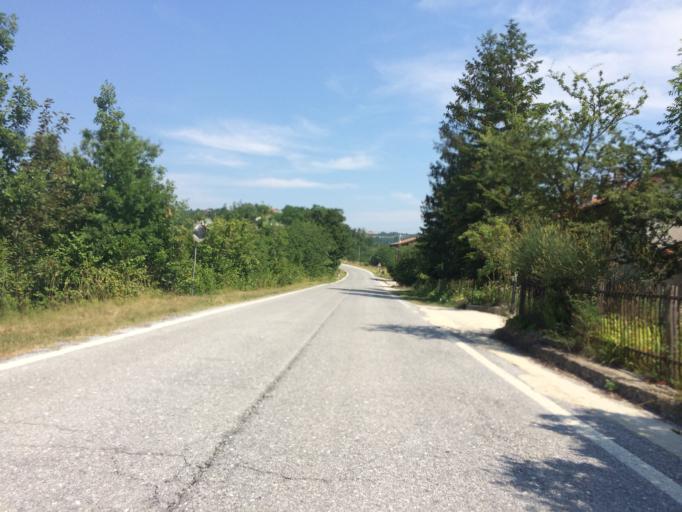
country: IT
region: Piedmont
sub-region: Provincia di Cuneo
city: Cissone
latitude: 44.5609
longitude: 8.0377
